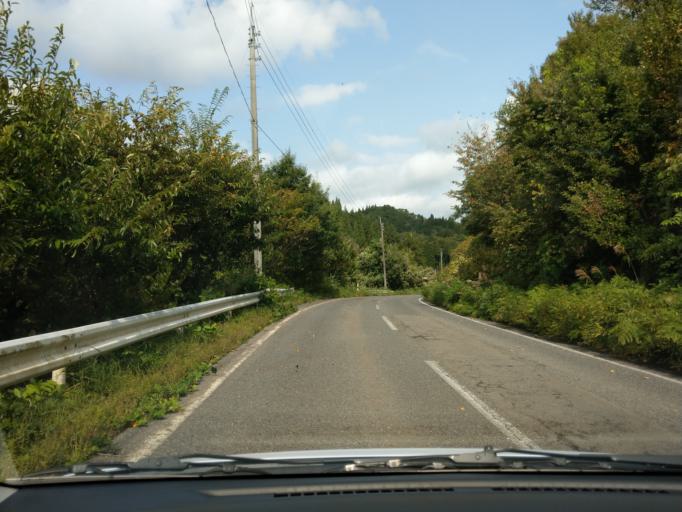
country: JP
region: Akita
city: Omagari
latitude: 39.4627
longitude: 140.3169
